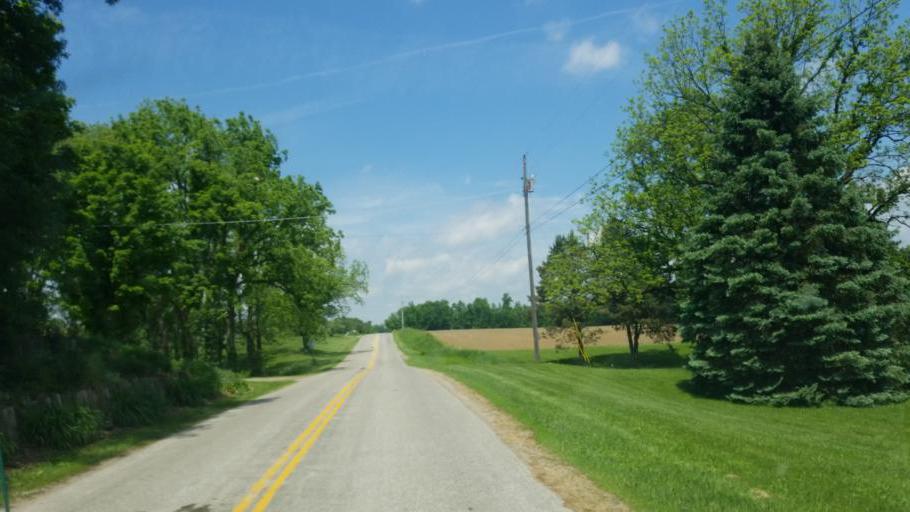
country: US
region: Ohio
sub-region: Ashland County
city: Ashland
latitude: 40.8283
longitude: -82.1749
